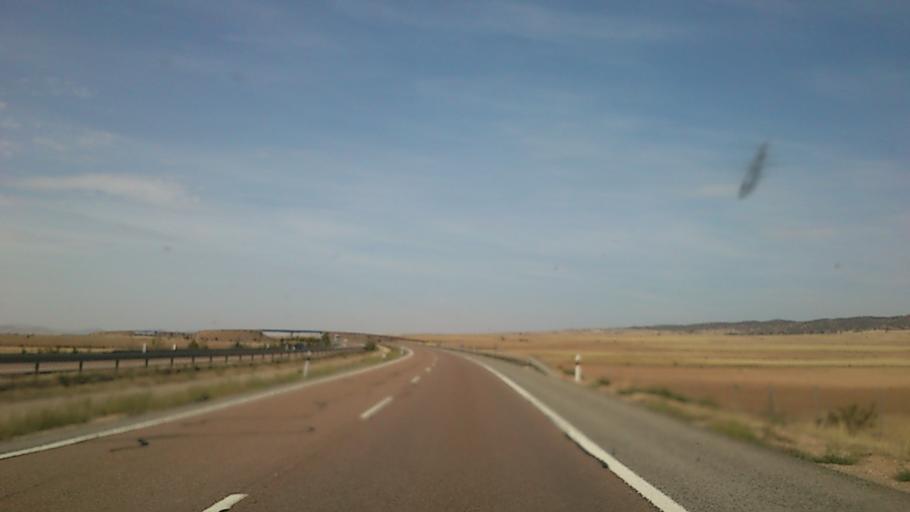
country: ES
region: Aragon
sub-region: Provincia de Teruel
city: Singra
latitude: 40.6711
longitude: -1.3140
